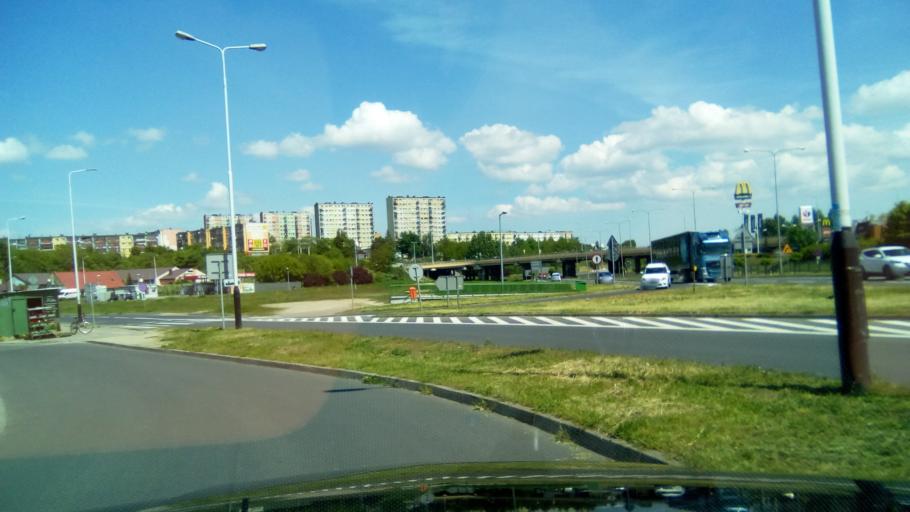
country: PL
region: Greater Poland Voivodeship
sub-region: Powiat gnieznienski
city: Gniezno
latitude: 52.5437
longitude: 17.6008
